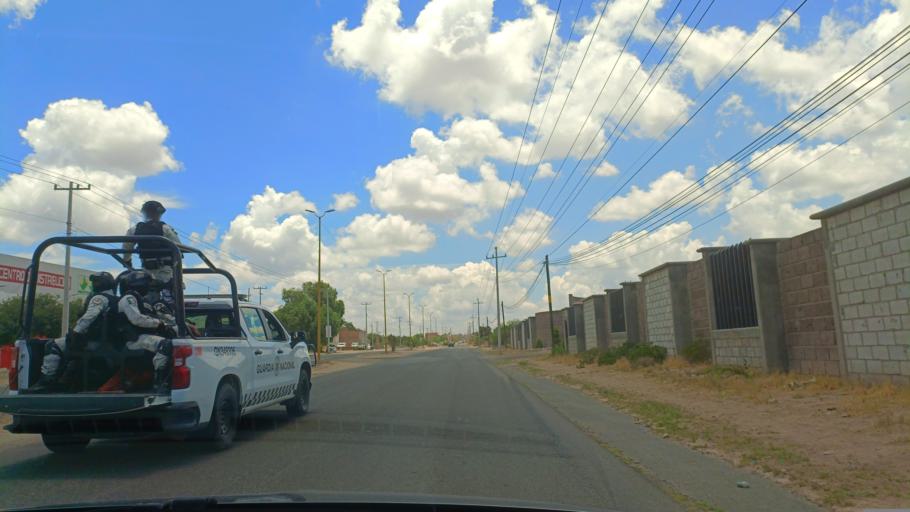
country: MX
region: Guanajuato
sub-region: San Luis de la Paz
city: San Ignacio
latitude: 21.2875
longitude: -100.5380
